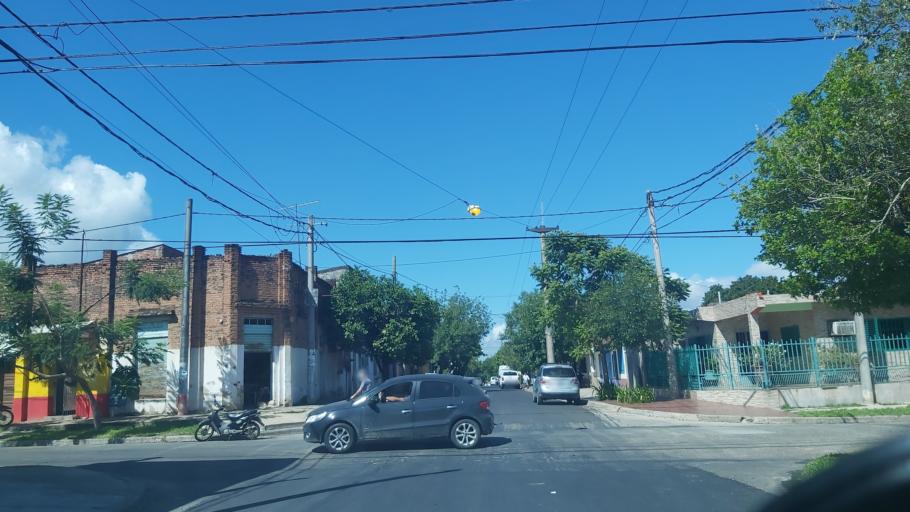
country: AR
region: Corrientes
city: Corrientes
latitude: -27.4803
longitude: -58.8477
